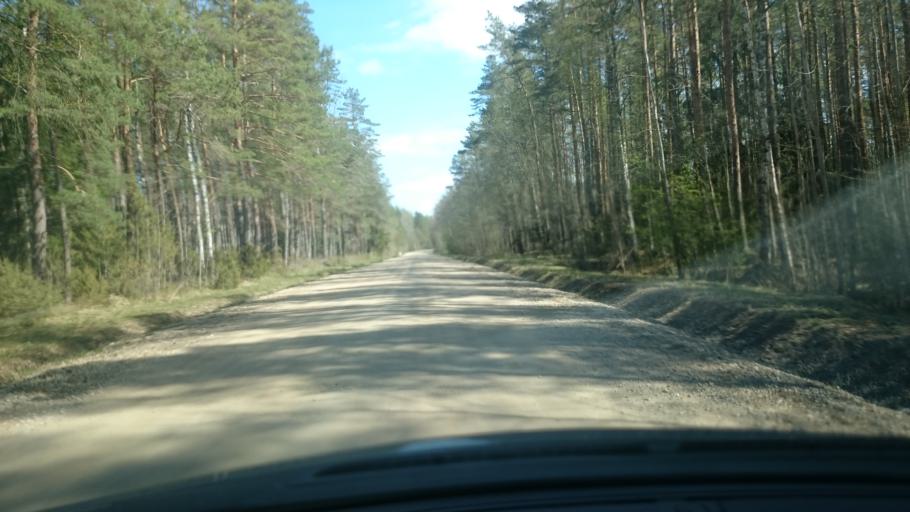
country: EE
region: Ida-Virumaa
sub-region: Sillamaee linn
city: Sillamae
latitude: 59.0811
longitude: 27.7336
